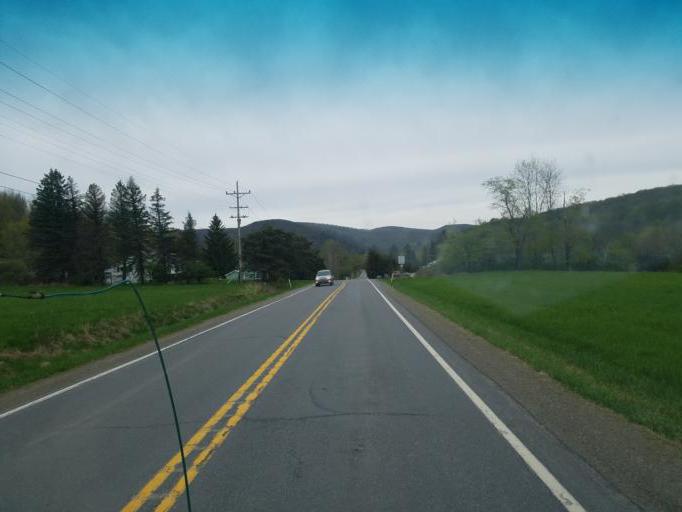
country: US
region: Pennsylvania
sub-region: Tioga County
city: Westfield
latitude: 41.9026
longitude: -77.5338
